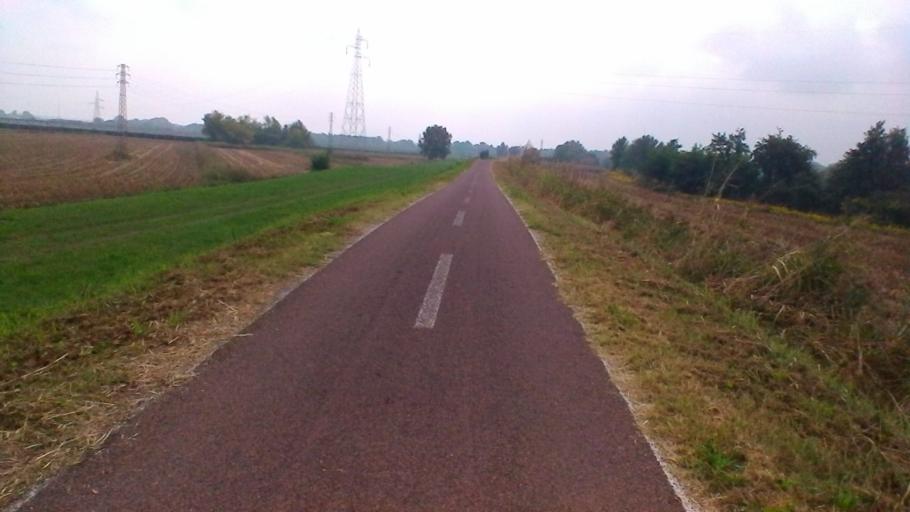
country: IT
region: Veneto
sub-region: Provincia di Verona
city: San Giovanni Lupatoto
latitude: 45.3933
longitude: 11.0595
